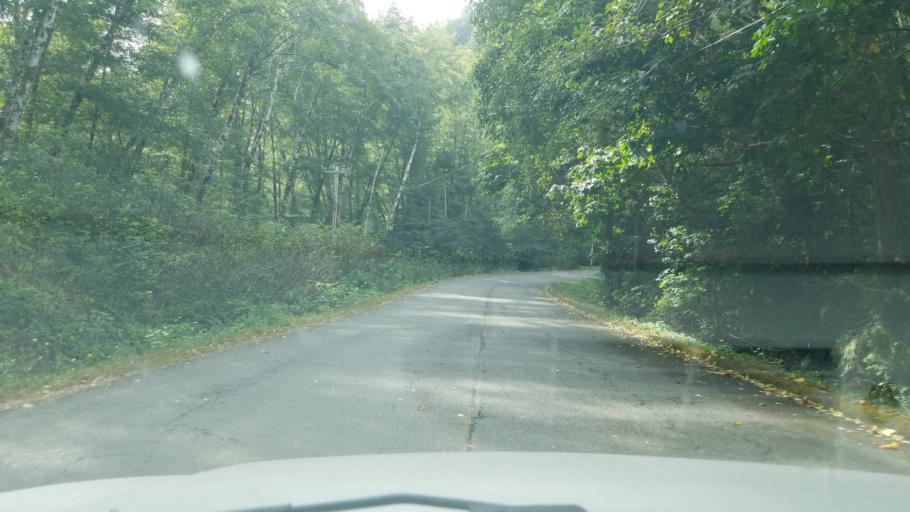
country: US
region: California
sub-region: Del Norte County
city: Bertsch-Oceanview
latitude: 41.5119
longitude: -124.0356
